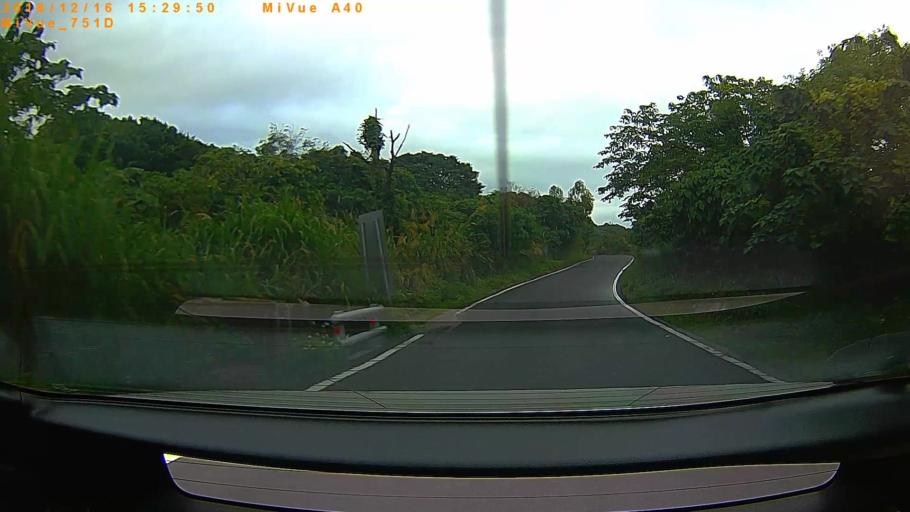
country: TW
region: Taiwan
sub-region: Hualien
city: Hualian
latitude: 23.9129
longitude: 121.5994
